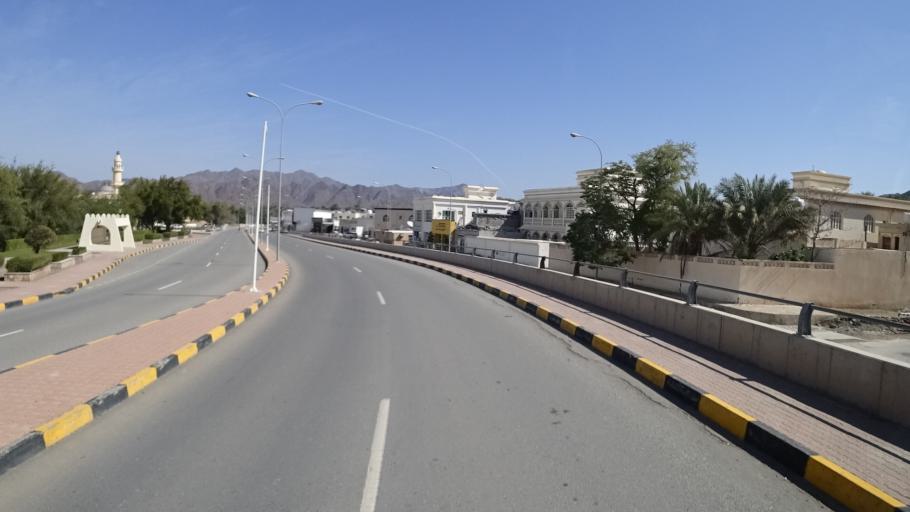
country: OM
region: Al Batinah
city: Rustaq
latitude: 23.3878
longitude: 57.4233
